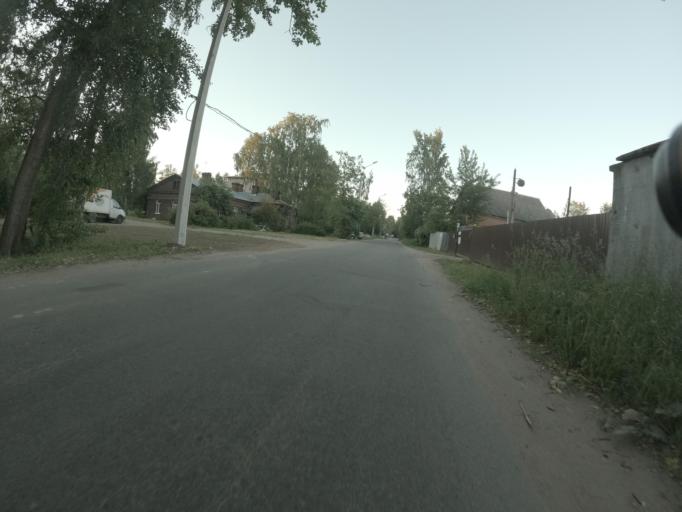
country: RU
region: St.-Petersburg
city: Krasnogvargeisky
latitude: 59.9753
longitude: 30.5085
